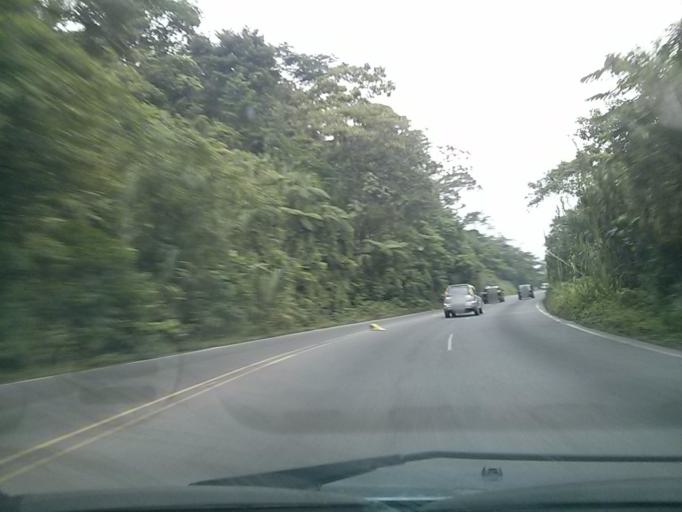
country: CR
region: San Jose
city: Dulce Nombre de Jesus
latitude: 10.1585
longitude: -83.9584
